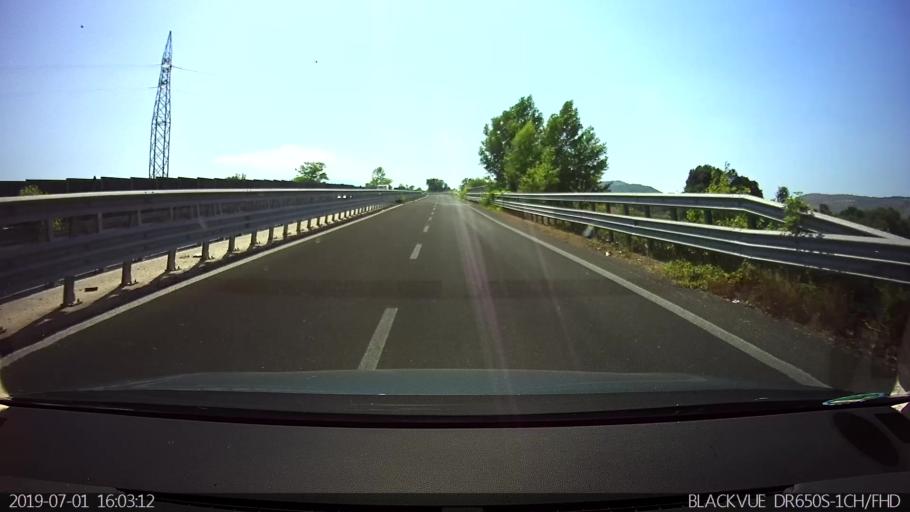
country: IT
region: Latium
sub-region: Provincia di Frosinone
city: Tecchiena
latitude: 41.6738
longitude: 13.3382
